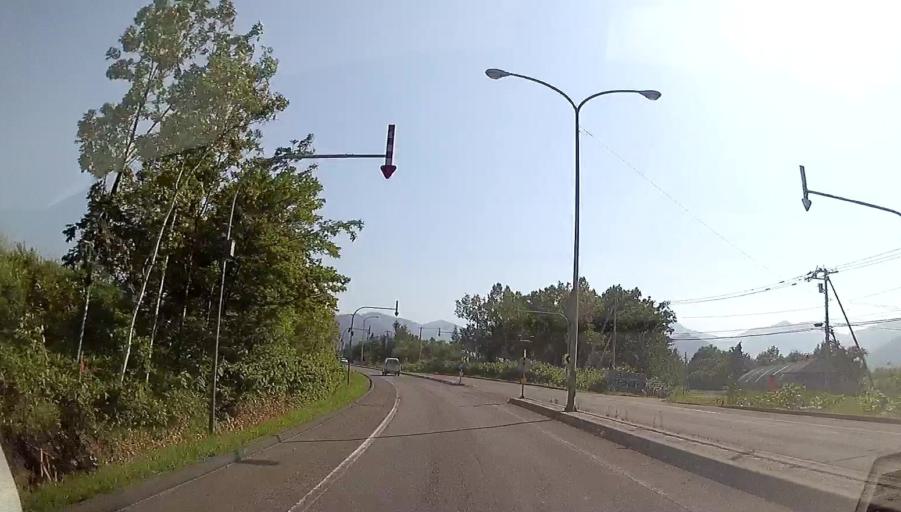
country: JP
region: Hokkaido
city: Otofuke
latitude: 42.9879
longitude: 142.8399
